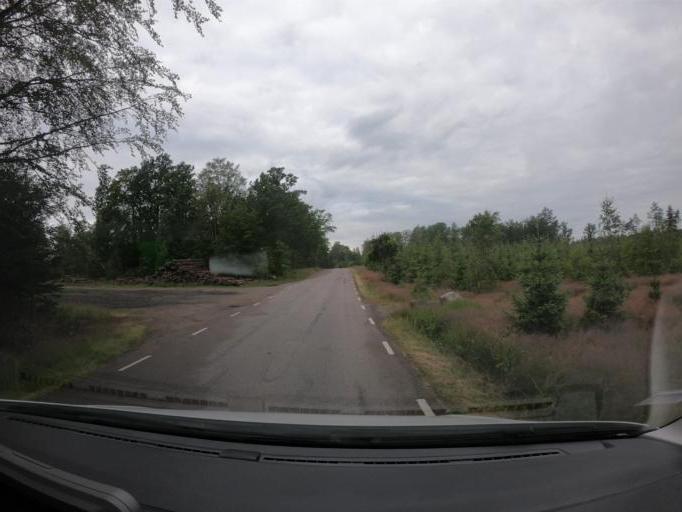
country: SE
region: Skane
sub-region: Orkelljunga Kommun
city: OErkelljunga
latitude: 56.2665
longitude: 13.1494
